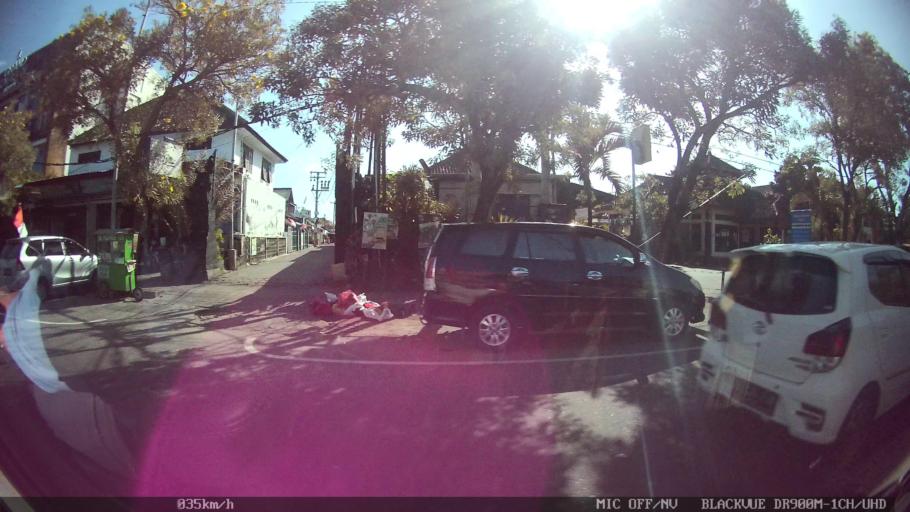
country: ID
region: Bali
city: Kelanabian
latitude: -8.7426
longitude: 115.1790
